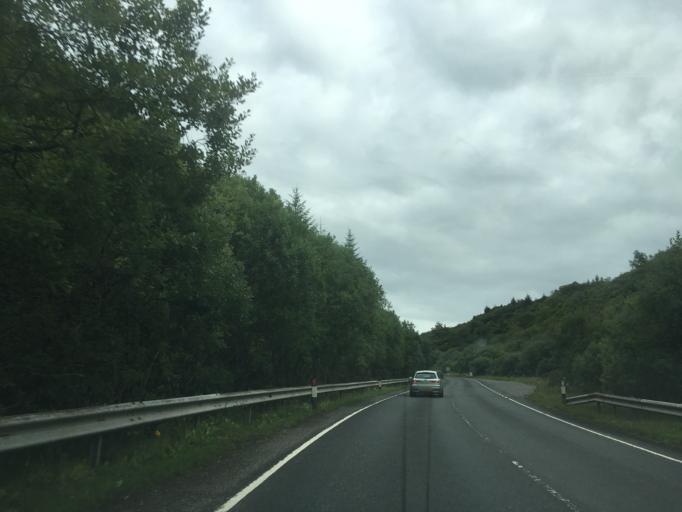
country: GB
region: Scotland
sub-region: Argyll and Bute
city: Oban
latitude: 56.3114
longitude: -5.4697
